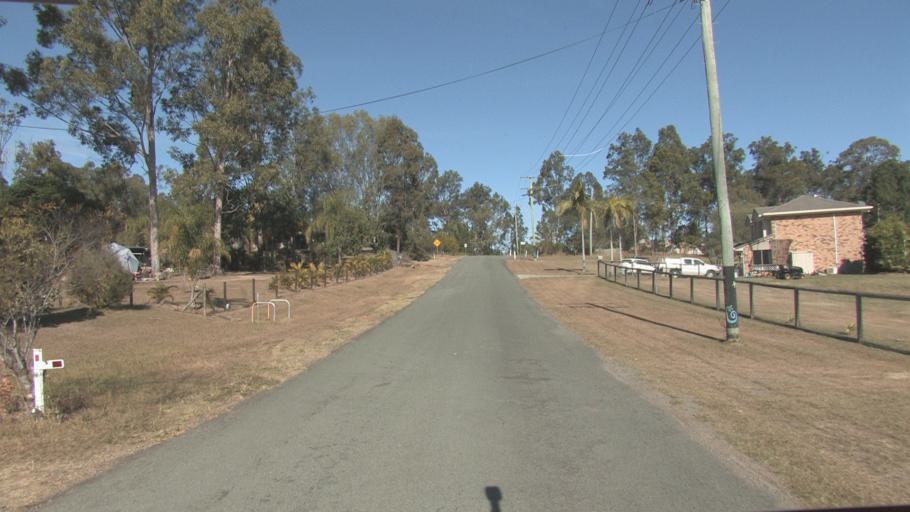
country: AU
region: Queensland
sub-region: Logan
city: Cedar Vale
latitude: -27.8538
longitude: 152.9859
